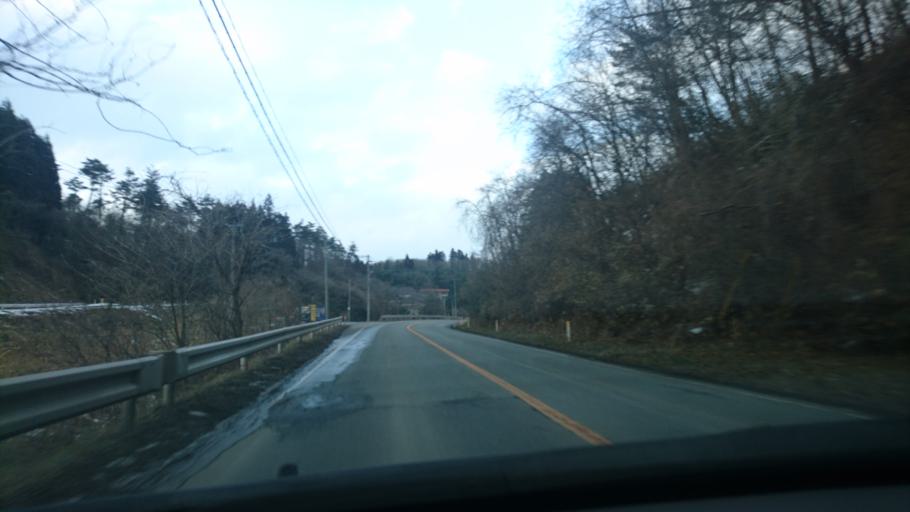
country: JP
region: Iwate
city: Ichinoseki
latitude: 38.9738
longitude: 141.3293
